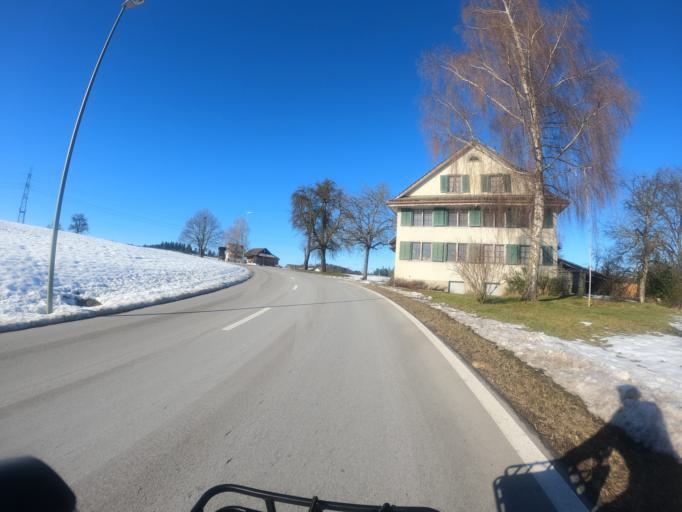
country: CH
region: Zurich
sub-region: Bezirk Affoltern
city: Hedingen
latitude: 47.2886
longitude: 8.4291
